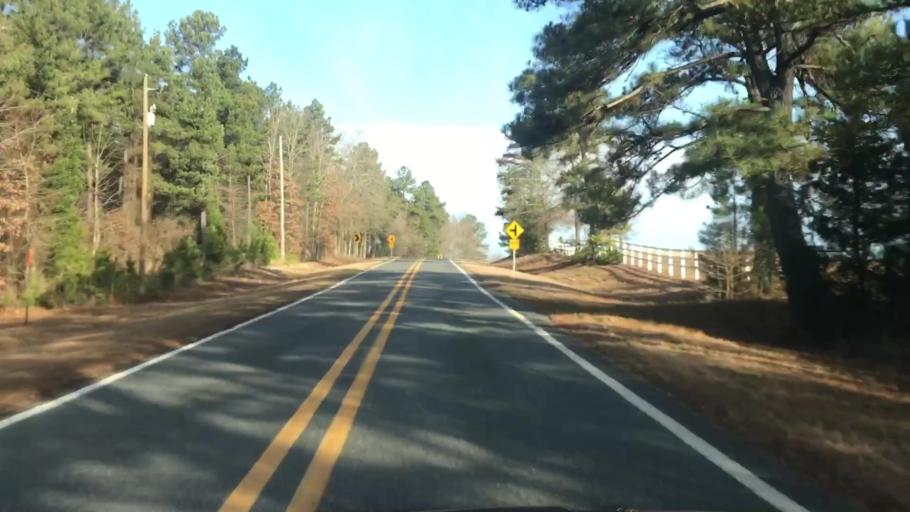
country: US
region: Arkansas
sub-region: Garland County
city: Rockwell
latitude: 34.4938
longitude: -93.2762
